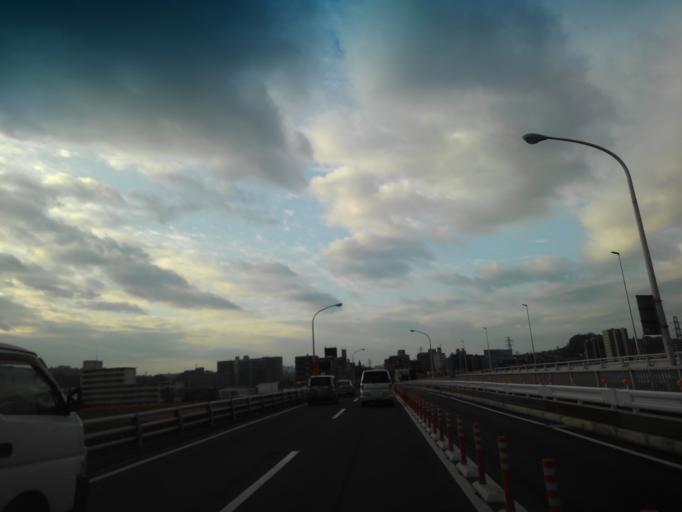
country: JP
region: Tokyo
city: Kokubunji
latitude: 35.6538
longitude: 139.4553
